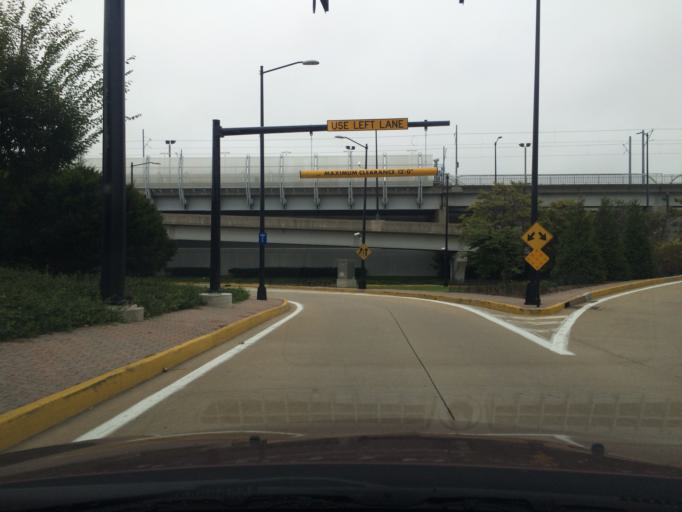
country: US
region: Missouri
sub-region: Saint Louis County
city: Woodson Terrace
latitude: 38.7406
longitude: -90.3655
